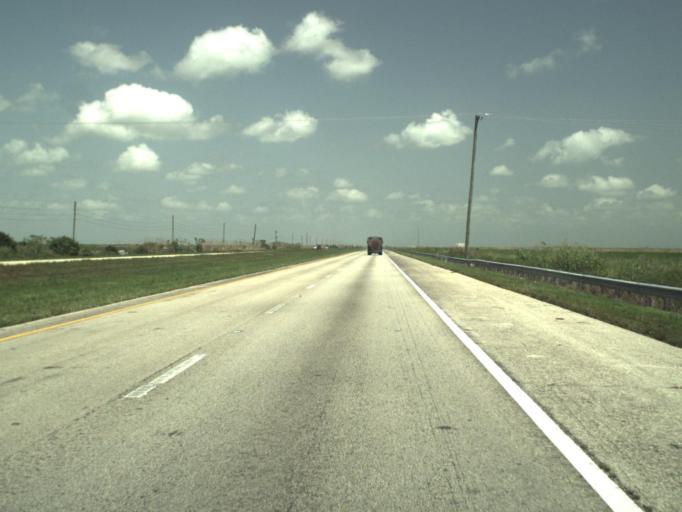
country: US
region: Florida
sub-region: Palm Beach County
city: Belle Glade Camp
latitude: 26.4050
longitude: -80.5918
